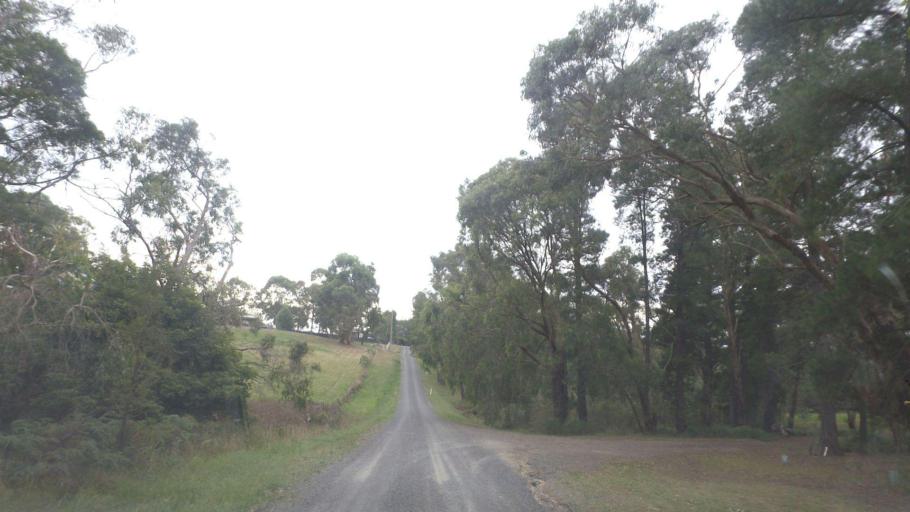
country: AU
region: Victoria
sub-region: Yarra Ranges
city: Mount Evelyn
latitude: -37.7598
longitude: 145.3952
